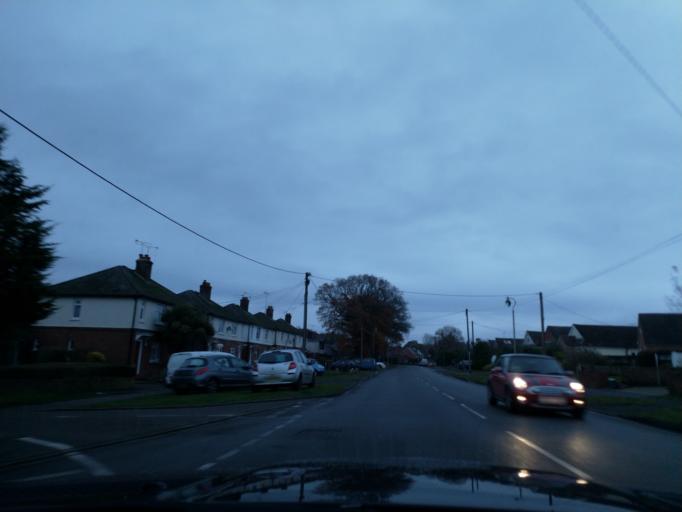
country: GB
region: England
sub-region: Hampshire
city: Farnborough
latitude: 51.2932
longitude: -0.7321
